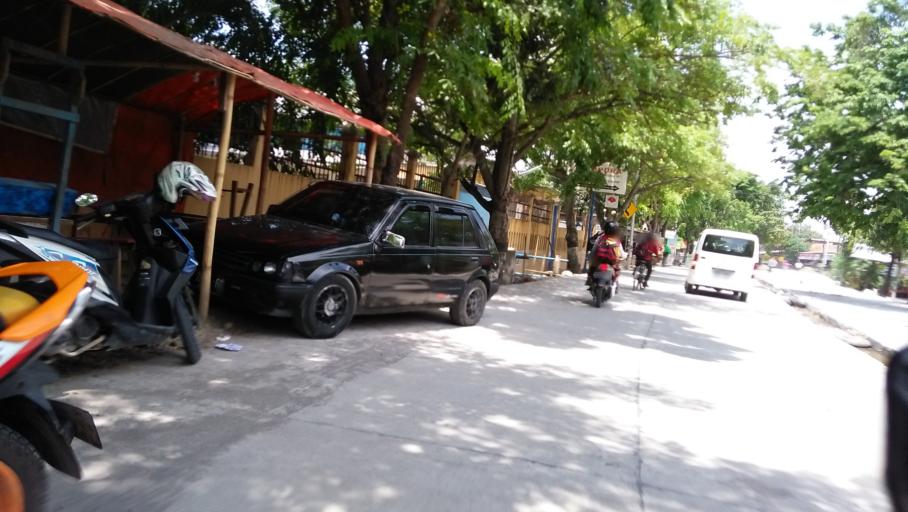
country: ID
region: Central Java
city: Mranggen
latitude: -6.9765
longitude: 110.4809
